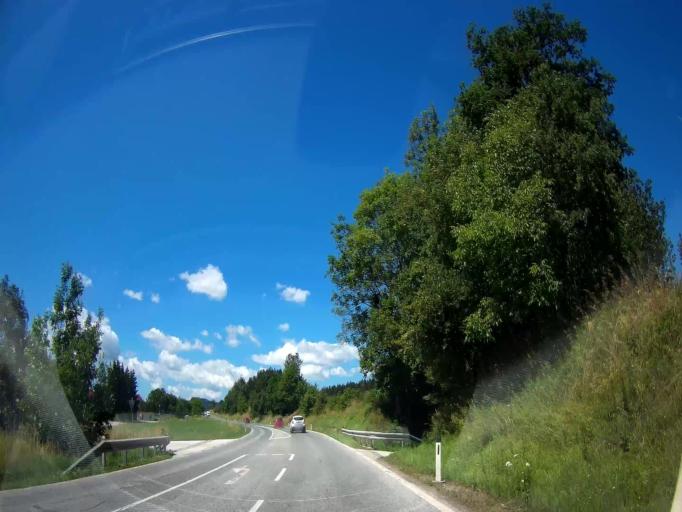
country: AT
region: Carinthia
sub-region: Politischer Bezirk Sankt Veit an der Glan
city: St. Georgen am Laengsee
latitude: 46.7627
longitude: 14.4165
